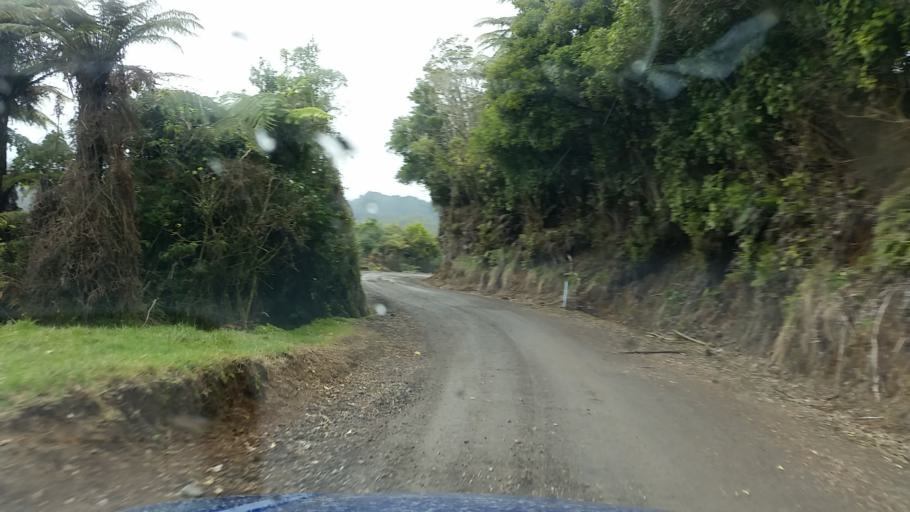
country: NZ
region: Taranaki
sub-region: South Taranaki District
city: Eltham
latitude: -39.1680
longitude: 174.6283
